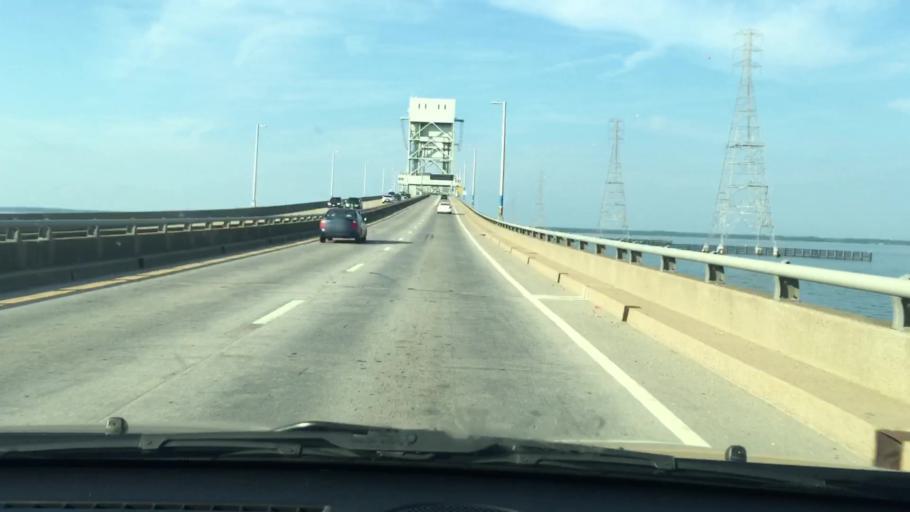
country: US
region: Virginia
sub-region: City of Newport News
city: Newport News
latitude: 37.0061
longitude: -76.4648
